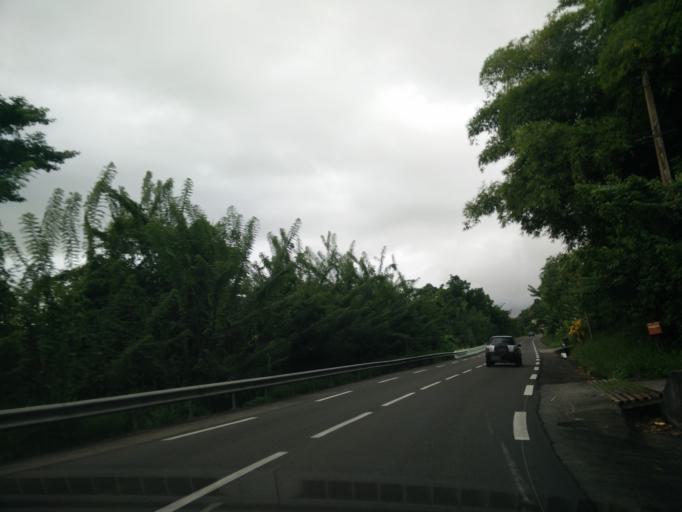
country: MQ
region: Martinique
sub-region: Martinique
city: Le Marin
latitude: 14.4851
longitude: -60.8607
